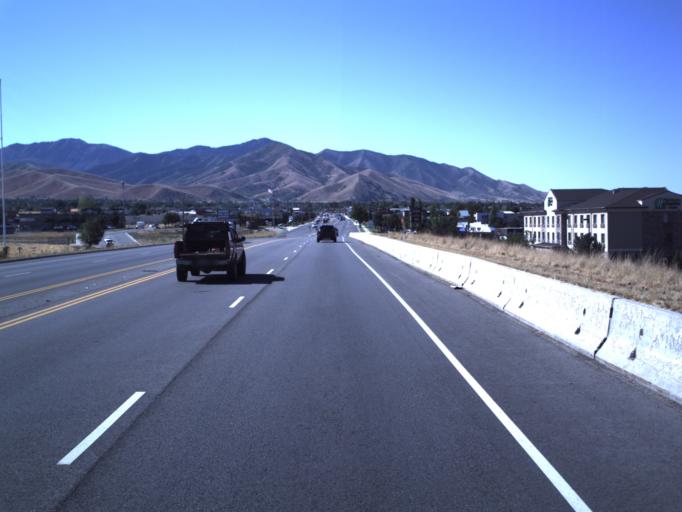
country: US
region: Utah
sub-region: Tooele County
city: Tooele
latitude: 40.5606
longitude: -112.2967
